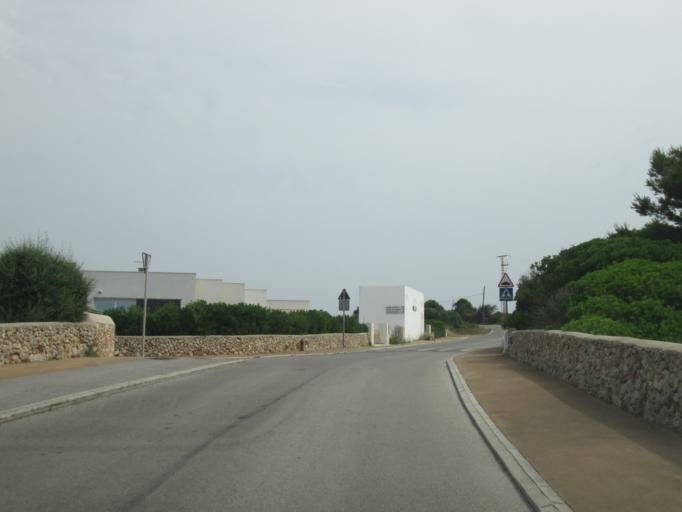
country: ES
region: Balearic Islands
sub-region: Illes Balears
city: Sant Lluis
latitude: 39.8369
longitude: 4.1939
